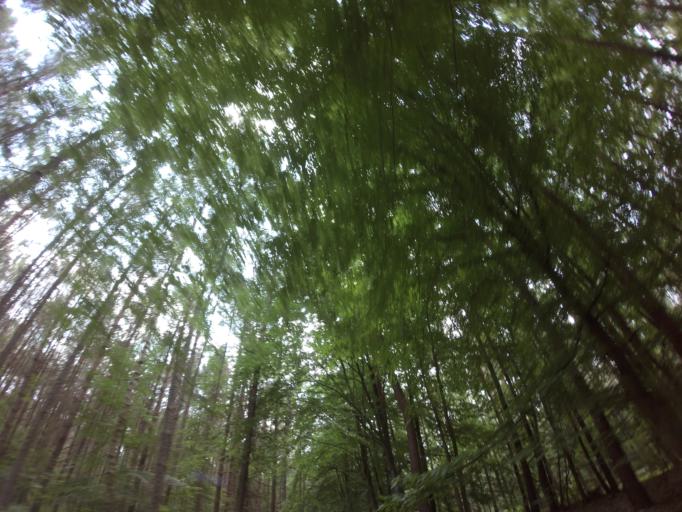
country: PL
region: West Pomeranian Voivodeship
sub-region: Powiat choszczenski
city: Bierzwnik
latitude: 53.0801
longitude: 15.6759
